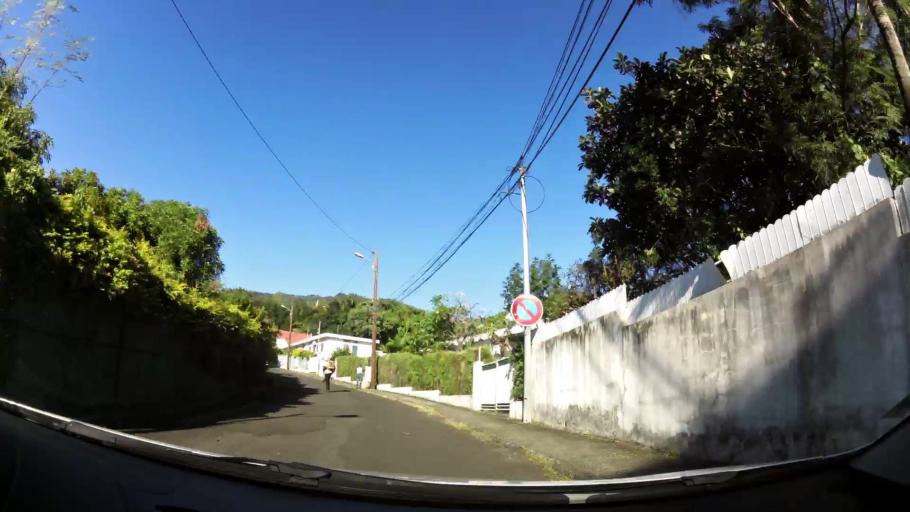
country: RE
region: Reunion
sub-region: Reunion
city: Saint-Denis
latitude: -20.8929
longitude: 55.4534
